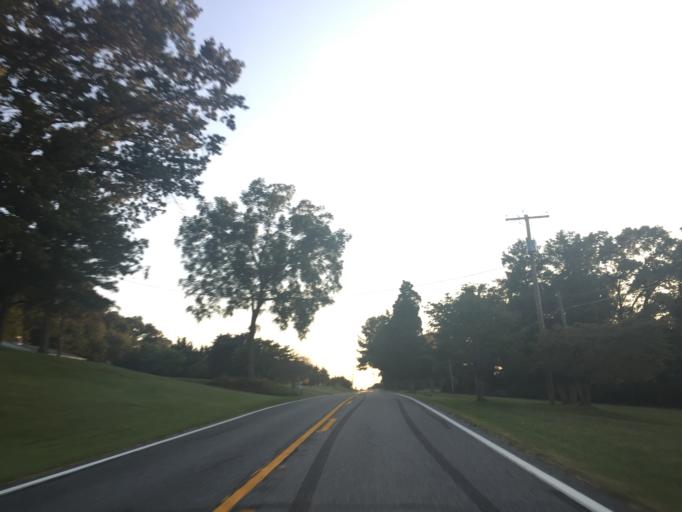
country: US
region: Pennsylvania
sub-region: York County
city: Susquehanna Trails
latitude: 39.6787
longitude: -76.3105
